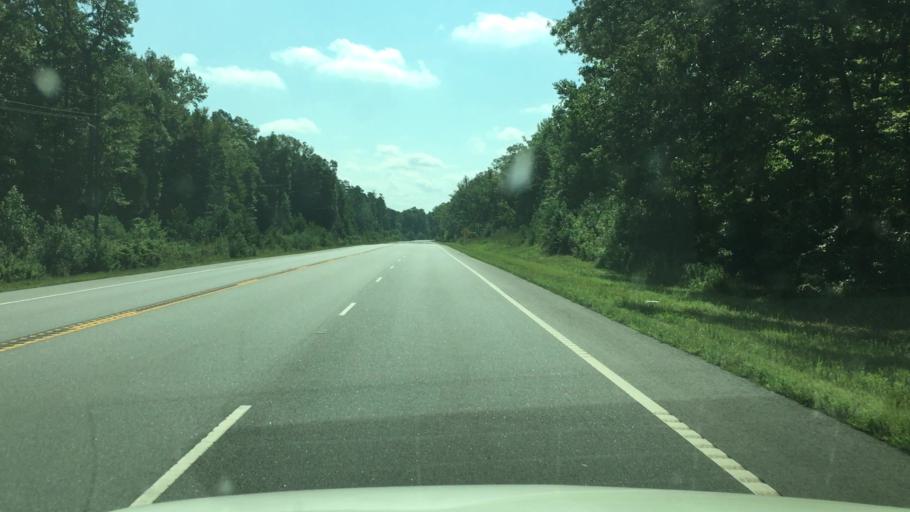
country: US
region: Arkansas
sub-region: Garland County
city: Rockwell
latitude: 34.5180
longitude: -93.3096
